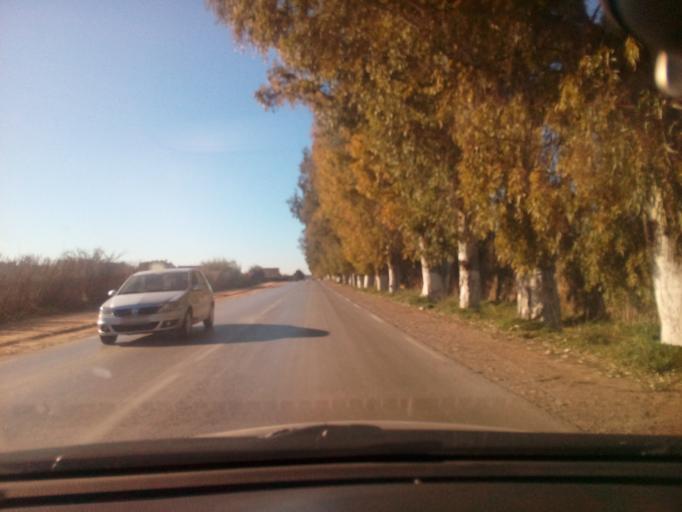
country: DZ
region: Mostaganem
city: Mostaganem
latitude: 35.8978
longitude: 0.2475
